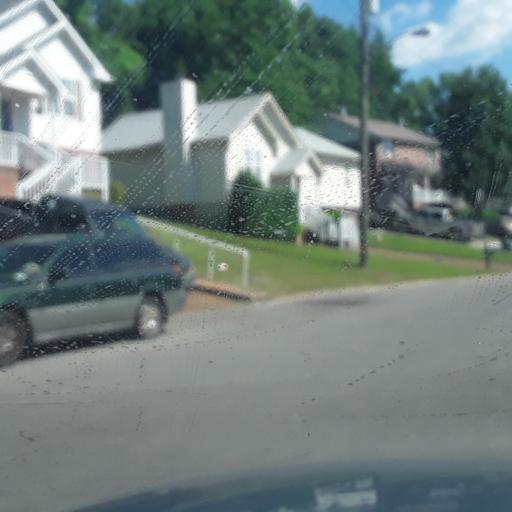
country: US
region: Tennessee
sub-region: Williamson County
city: Brentwood Estates
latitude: 36.0340
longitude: -86.7064
